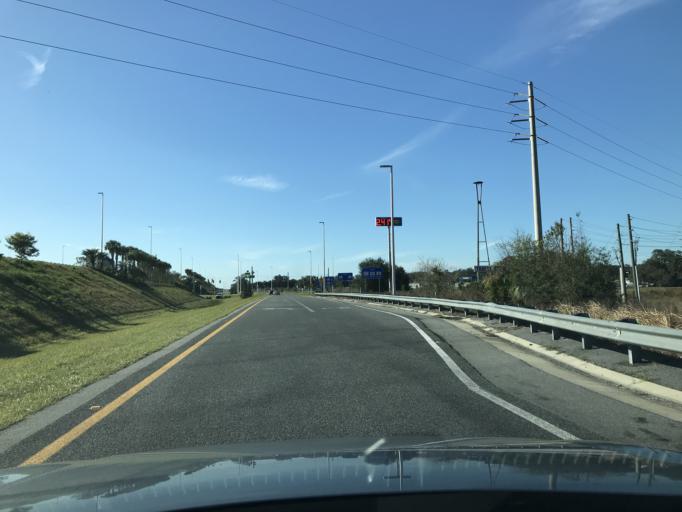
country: US
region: Florida
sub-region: Sumter County
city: Bushnell
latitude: 28.6706
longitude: -82.1421
